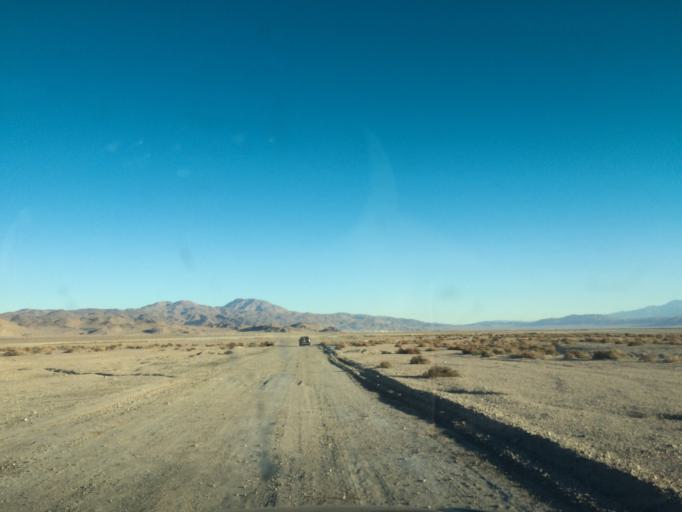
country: US
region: California
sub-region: San Bernardino County
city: Searles Valley
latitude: 35.6474
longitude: -117.3767
